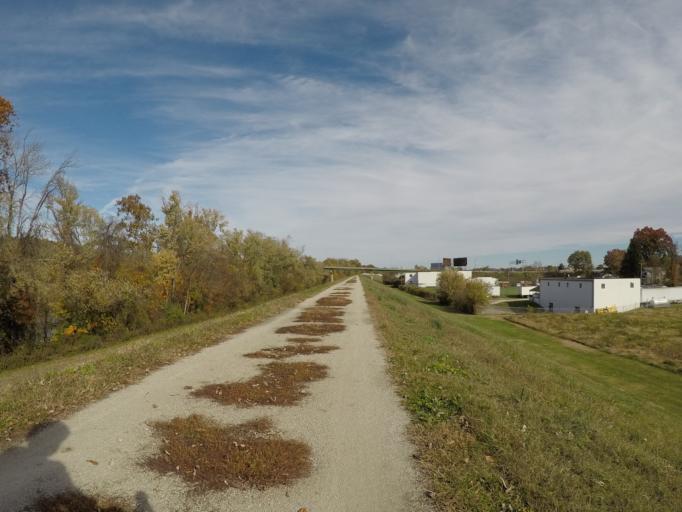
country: US
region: West Virginia
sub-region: Cabell County
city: Huntington
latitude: 38.4129
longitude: -82.4881
